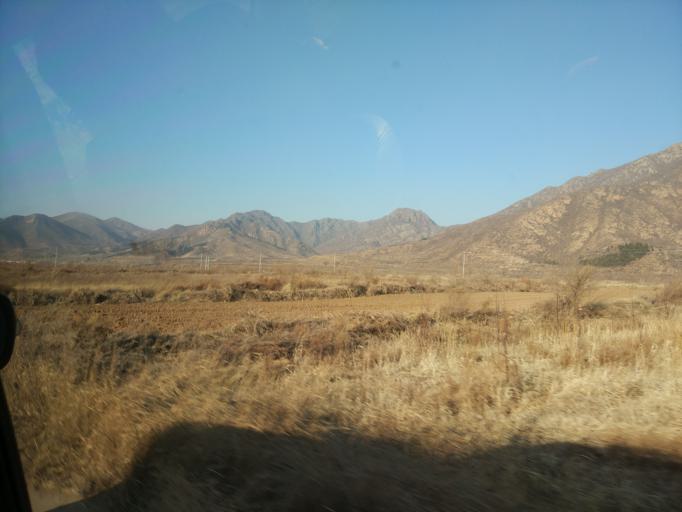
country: CN
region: Hebei
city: Xiwanzi
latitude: 40.8299
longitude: 115.5324
